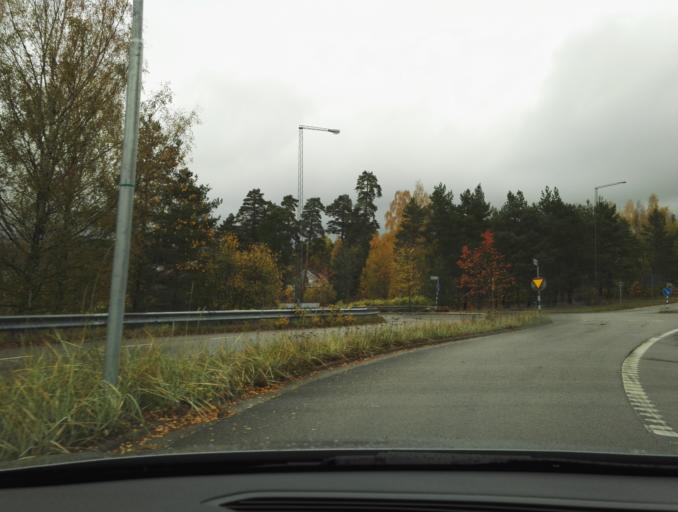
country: SE
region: Kronoberg
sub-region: Vaxjo Kommun
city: Vaexjoe
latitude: 56.8828
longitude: 14.7556
